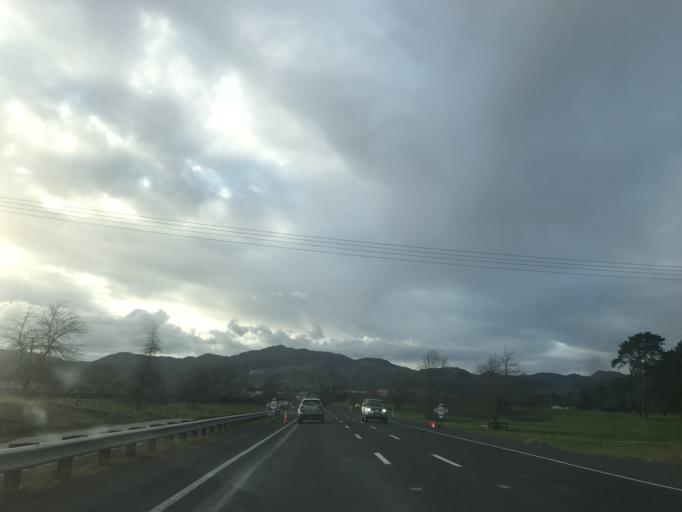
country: NZ
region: Waikato
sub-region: Hauraki District
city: Waihi
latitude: -37.4027
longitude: 175.8558
